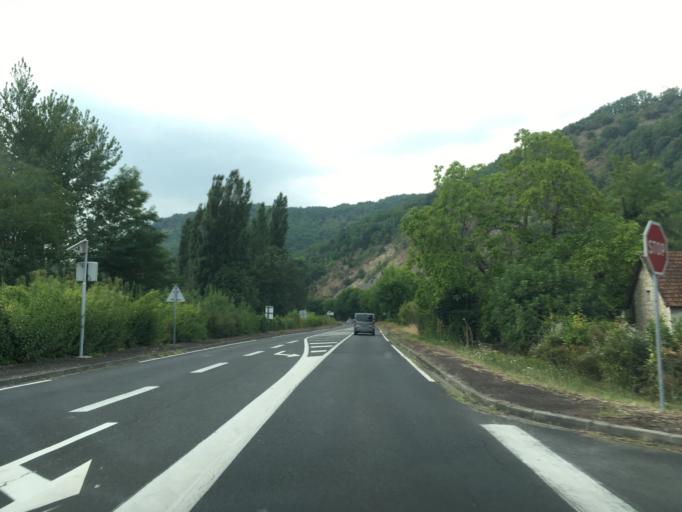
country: FR
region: Midi-Pyrenees
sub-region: Departement du Lot
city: Souillac
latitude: 44.8870
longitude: 1.4061
